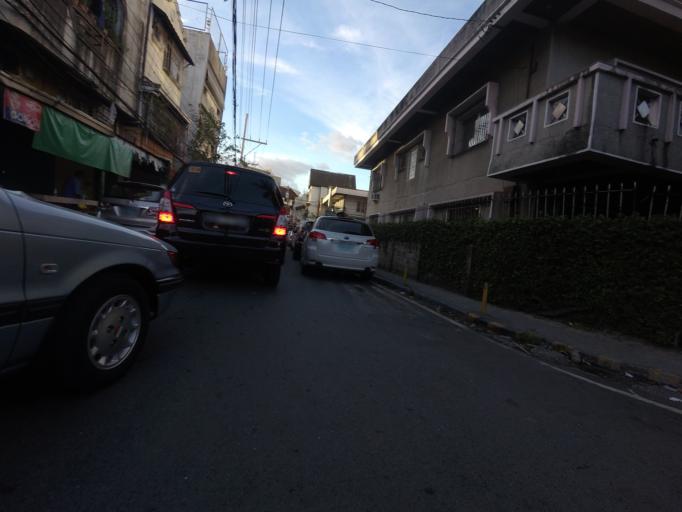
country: PH
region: Metro Manila
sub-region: San Juan
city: San Juan
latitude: 14.6034
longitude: 121.0384
